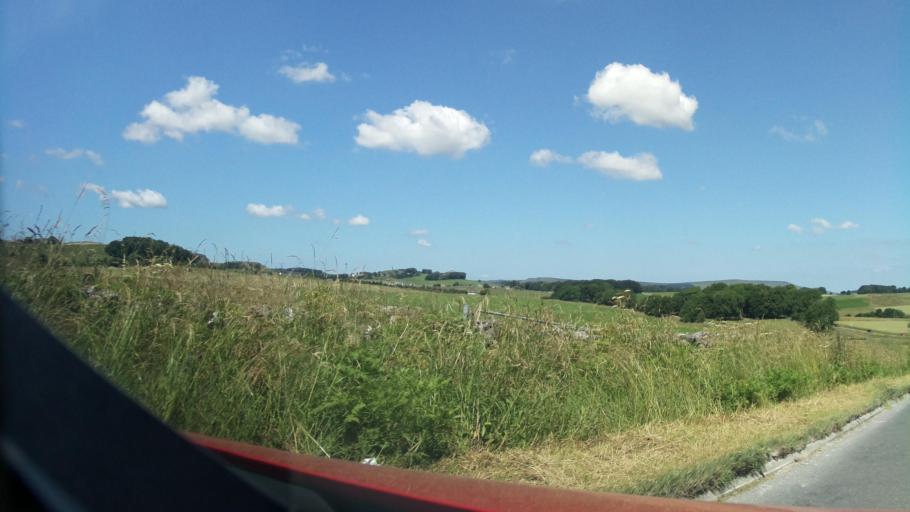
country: GB
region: England
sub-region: Derbyshire
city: Buxton
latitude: 53.2225
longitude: -1.8725
